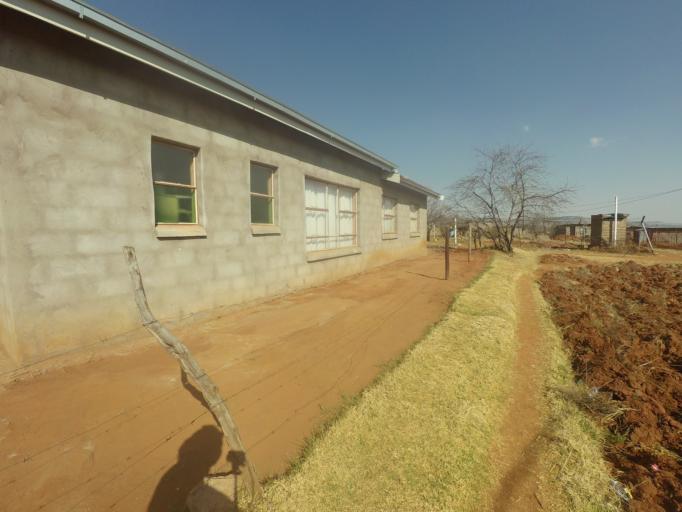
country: LS
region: Leribe
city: Maputsoe
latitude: -28.8984
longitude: 27.9193
